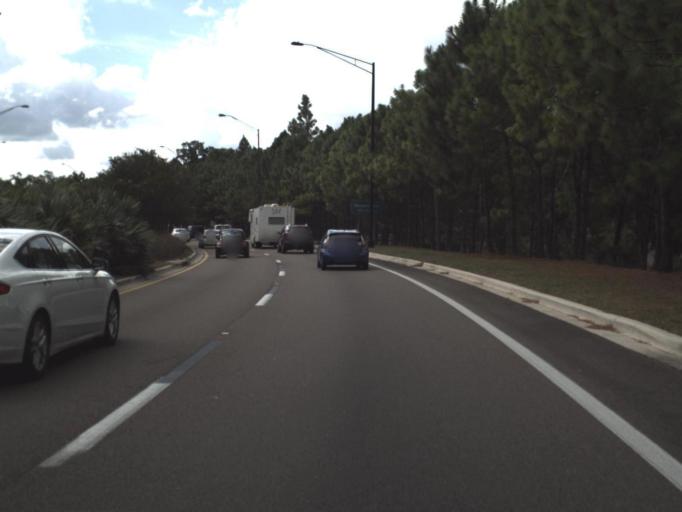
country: US
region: Florida
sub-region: Polk County
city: Lakeland
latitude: 28.0489
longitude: -81.9511
